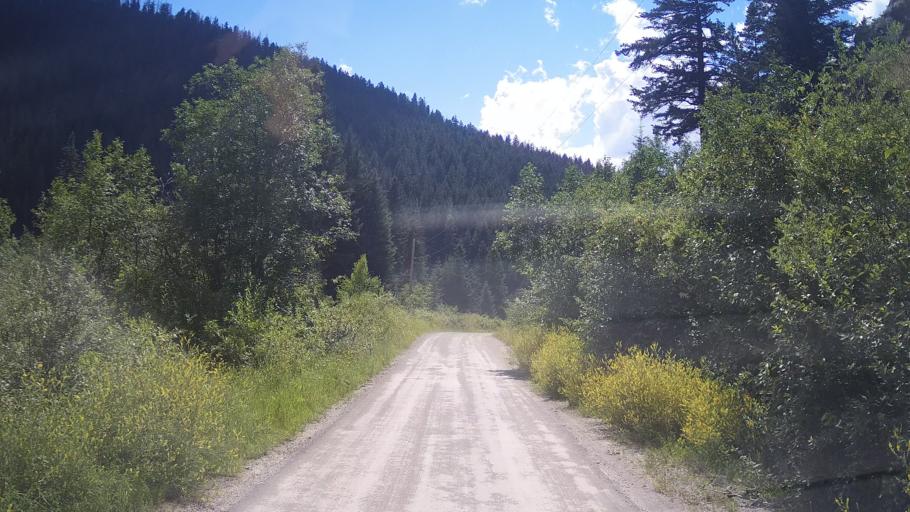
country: CA
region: British Columbia
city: Lillooet
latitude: 51.2566
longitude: -122.0005
